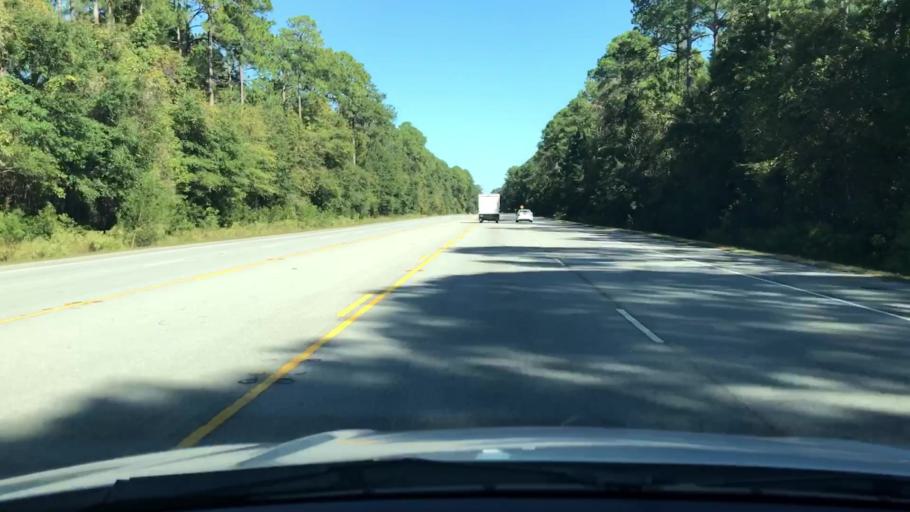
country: US
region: South Carolina
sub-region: Beaufort County
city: Burton
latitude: 32.4198
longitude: -80.7410
